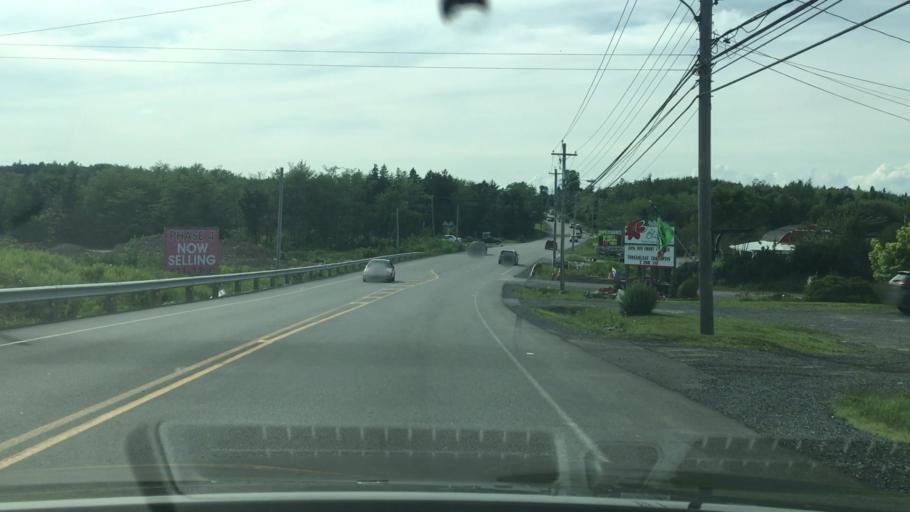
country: CA
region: Nova Scotia
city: Dartmouth
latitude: 44.7283
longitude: -63.7483
